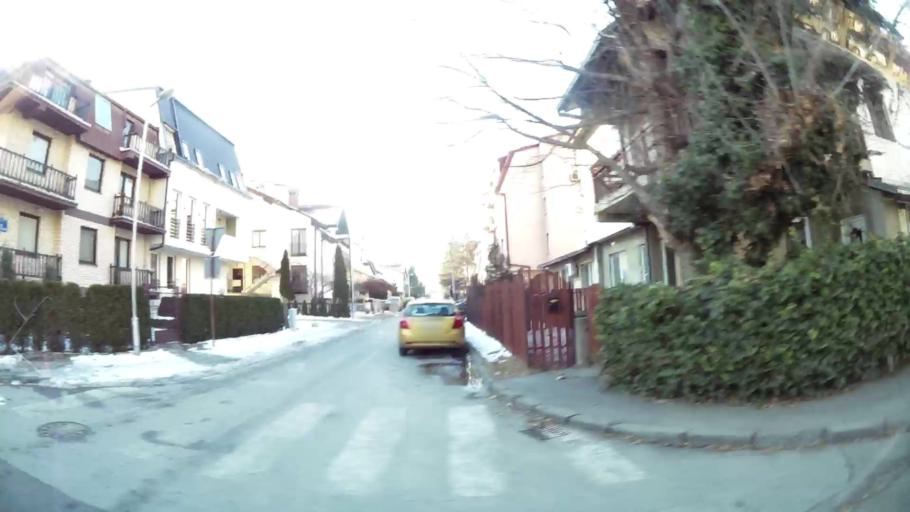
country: MK
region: Karpos
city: Skopje
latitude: 41.9948
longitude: 21.4032
